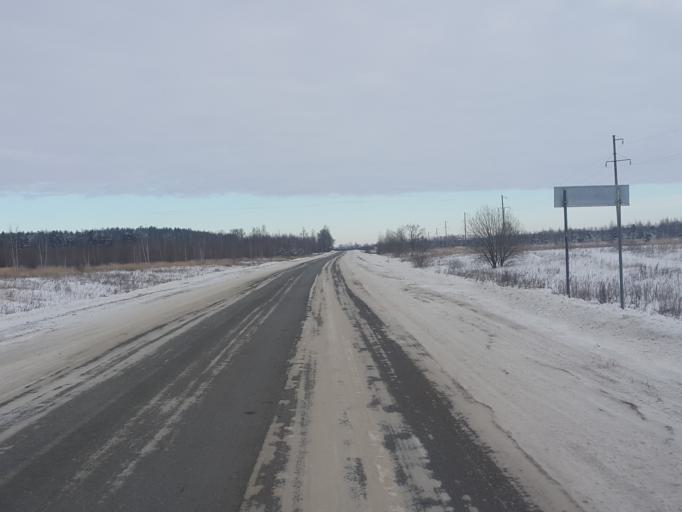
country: RU
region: Tambov
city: Platonovka
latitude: 52.8660
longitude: 41.8539
